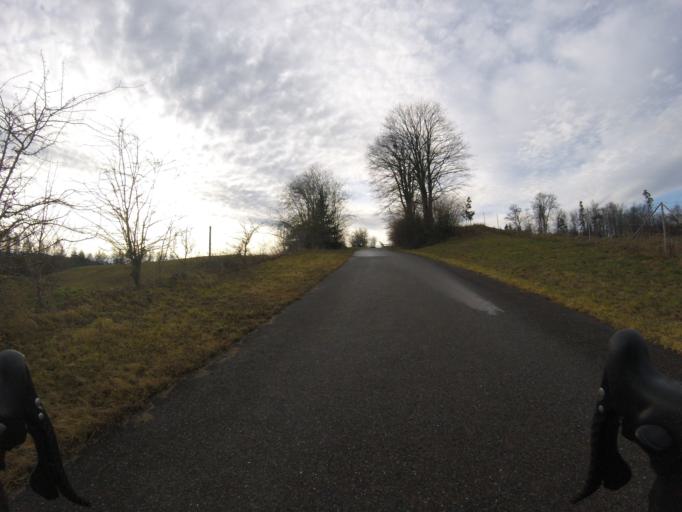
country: CH
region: Fribourg
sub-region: Sense District
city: Flamatt
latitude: 46.9124
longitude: 7.3535
